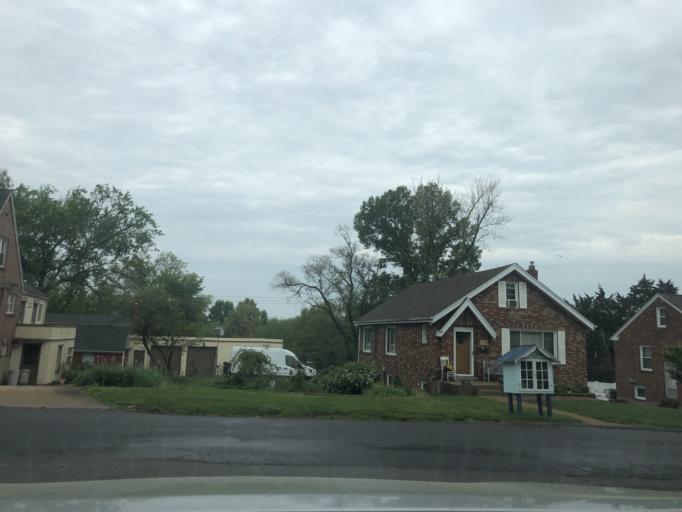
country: US
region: Missouri
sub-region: Saint Louis County
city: Affton
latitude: 38.5489
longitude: -90.3206
